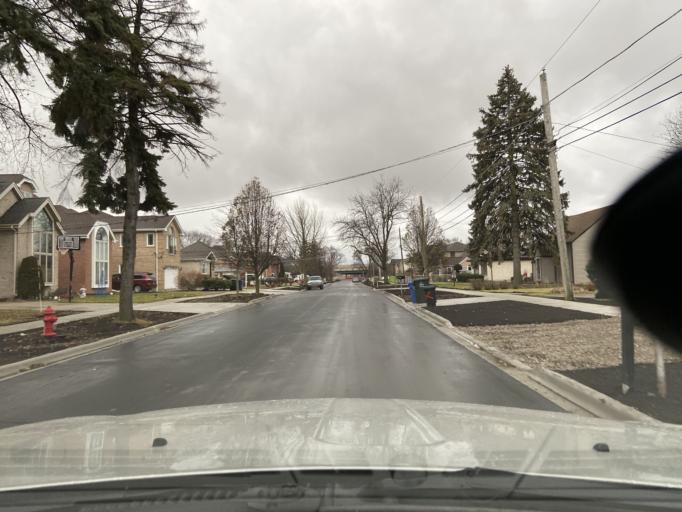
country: US
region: Illinois
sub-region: Cook County
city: Rosemont
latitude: 42.0121
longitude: -87.9032
